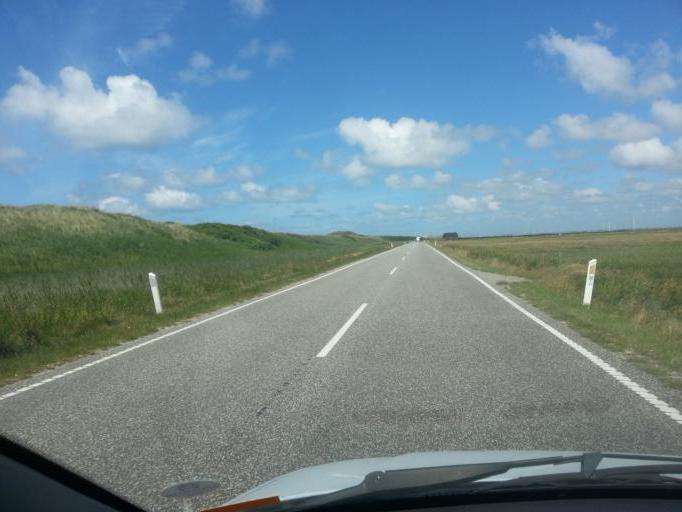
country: DK
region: Central Jutland
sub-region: Lemvig Kommune
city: Harboore
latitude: 56.3910
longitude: 8.1216
